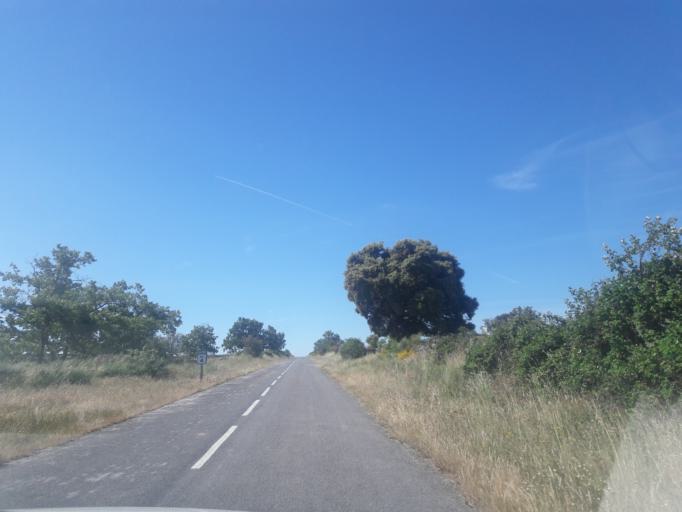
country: ES
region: Castille and Leon
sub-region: Provincia de Salamanca
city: Lumbrales
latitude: 40.9703
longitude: -6.7268
